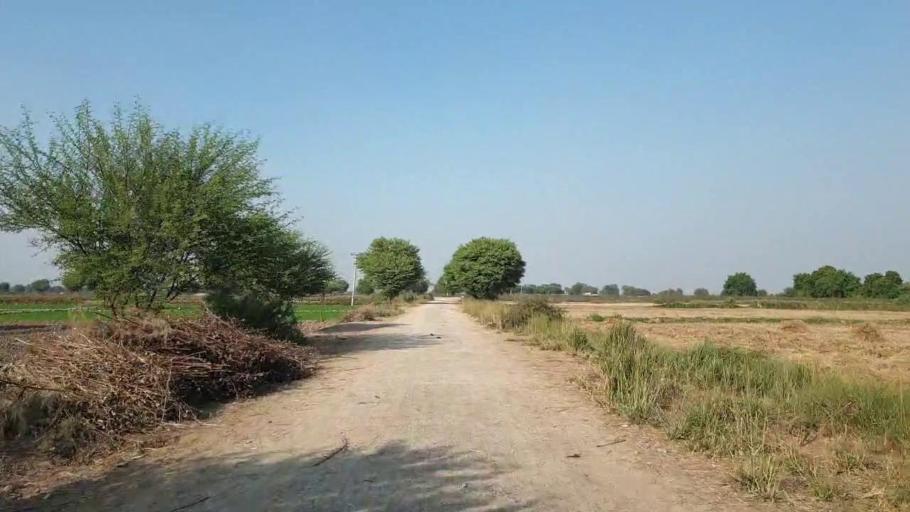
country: PK
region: Sindh
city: Sehwan
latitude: 26.4561
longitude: 67.8158
